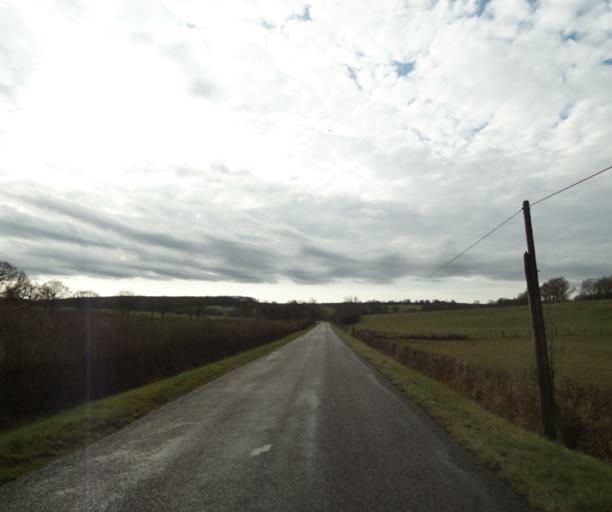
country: FR
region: Auvergne
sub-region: Departement de l'Allier
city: Toulon-sur-Allier
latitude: 46.5279
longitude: 3.4100
